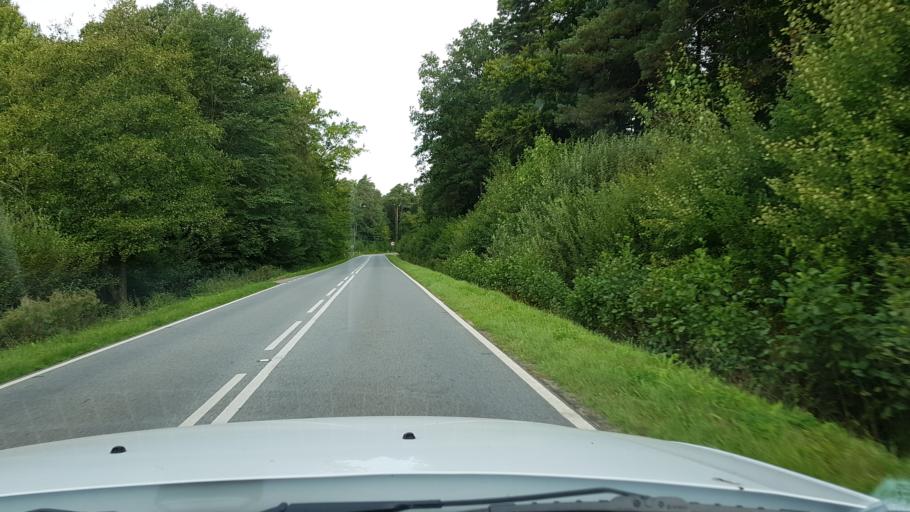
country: PL
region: West Pomeranian Voivodeship
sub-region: Powiat slawienski
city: Slawno
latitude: 54.3809
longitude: 16.6216
